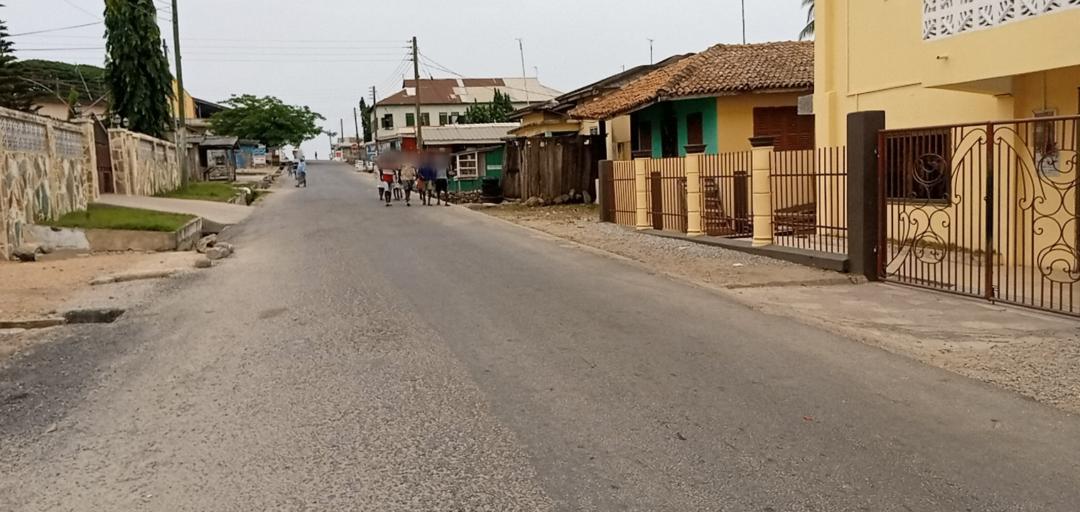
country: GH
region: Central
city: Winneba
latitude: 5.3469
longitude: -0.6244
